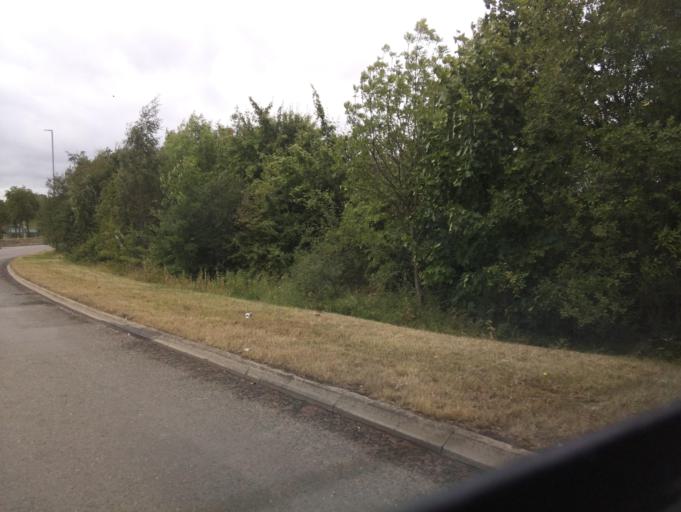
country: GB
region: England
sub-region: Nottinghamshire
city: Awsworth
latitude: 52.9802
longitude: -1.2917
